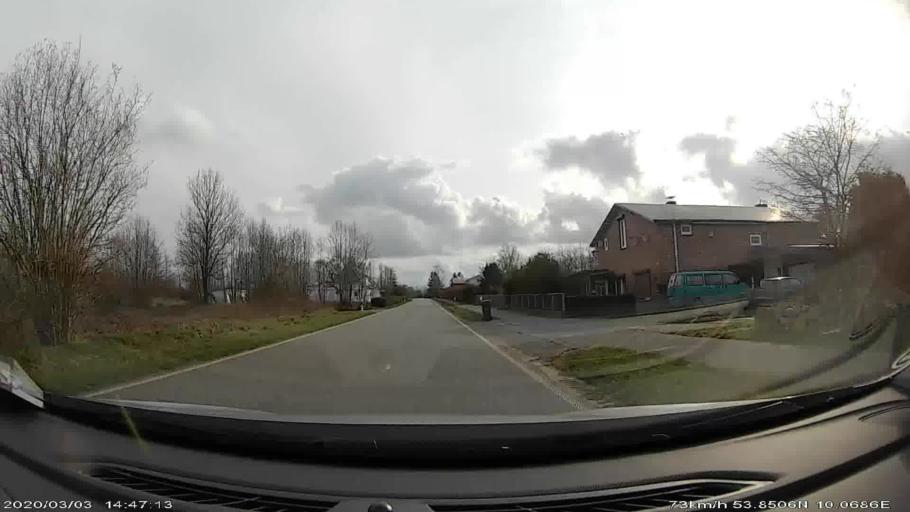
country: DE
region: Schleswig-Holstein
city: Huttblek
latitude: 53.8504
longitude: 10.0688
